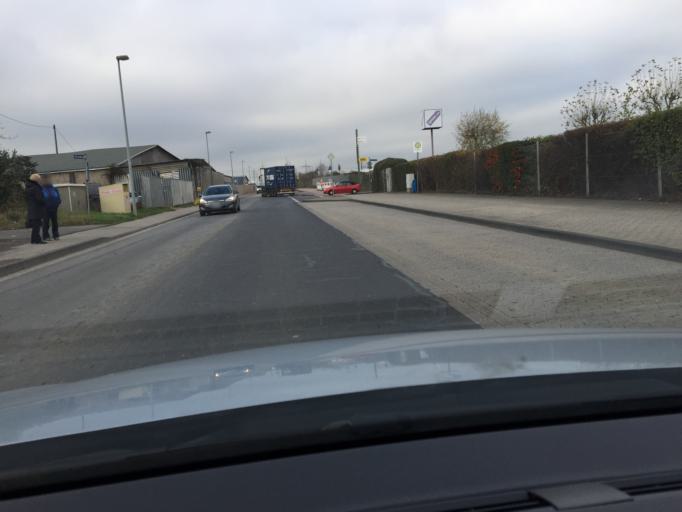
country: DE
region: Rheinland-Pfalz
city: Koblenz
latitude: 50.3781
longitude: 7.5945
